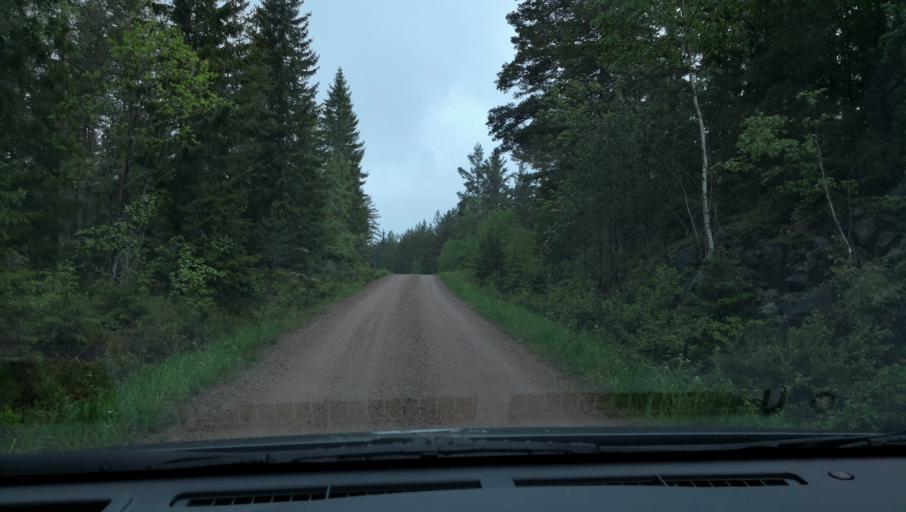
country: SE
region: Uppsala
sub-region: Enkopings Kommun
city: Orsundsbro
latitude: 59.9340
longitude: 17.3248
